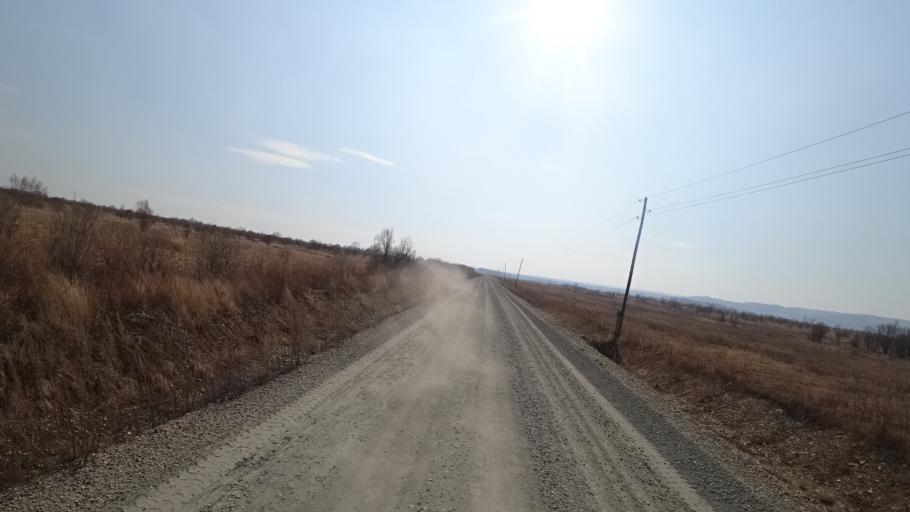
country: RU
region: Amur
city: Novobureyskiy
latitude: 49.8136
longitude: 129.9730
